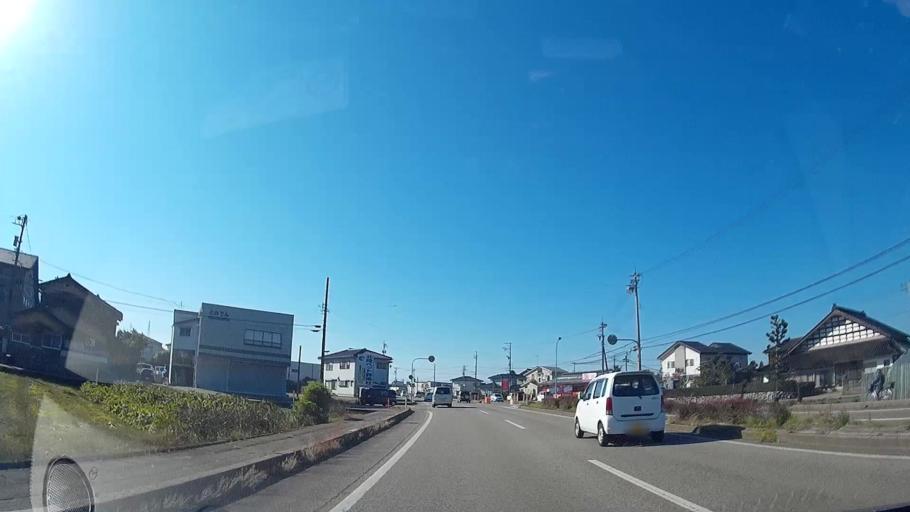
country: JP
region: Toyama
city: Takaoka
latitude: 36.6913
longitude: 136.9782
